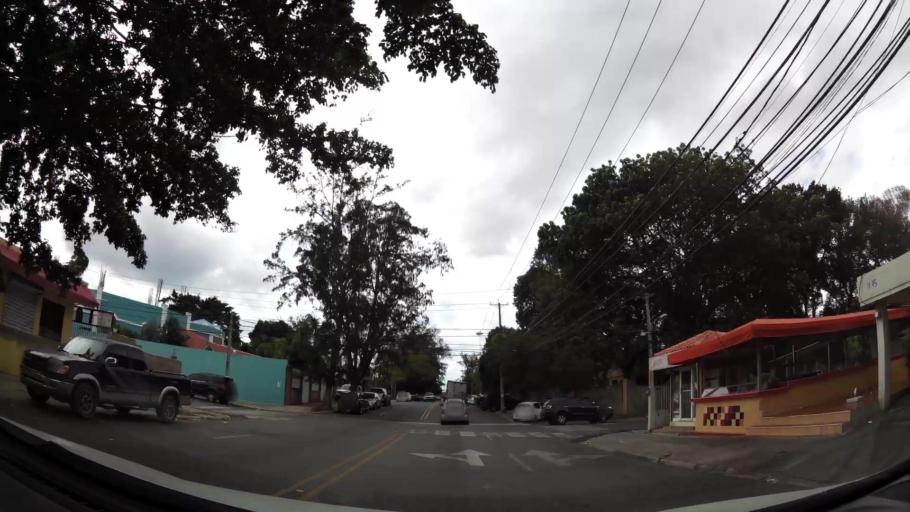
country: DO
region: Nacional
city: Bella Vista
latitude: 18.4734
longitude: -69.9577
